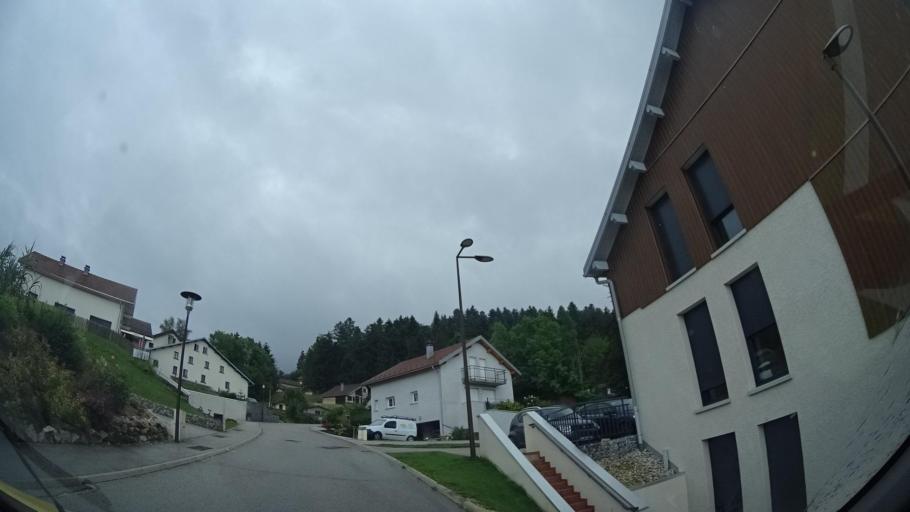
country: FR
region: Franche-Comte
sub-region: Departement du Doubs
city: Les Fourgs
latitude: 46.8261
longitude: 6.3386
